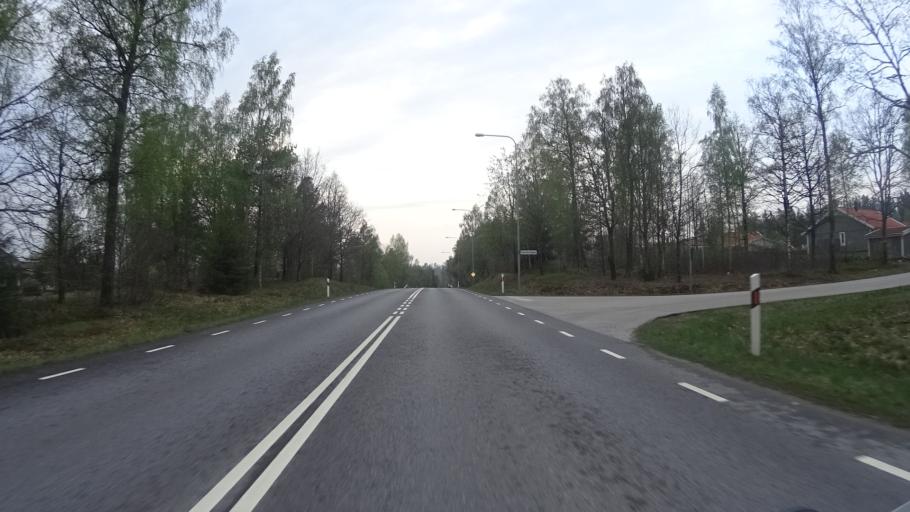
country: SE
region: Kronoberg
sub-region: Ljungby Kommun
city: Ljungby
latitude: 56.8331
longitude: 13.9737
